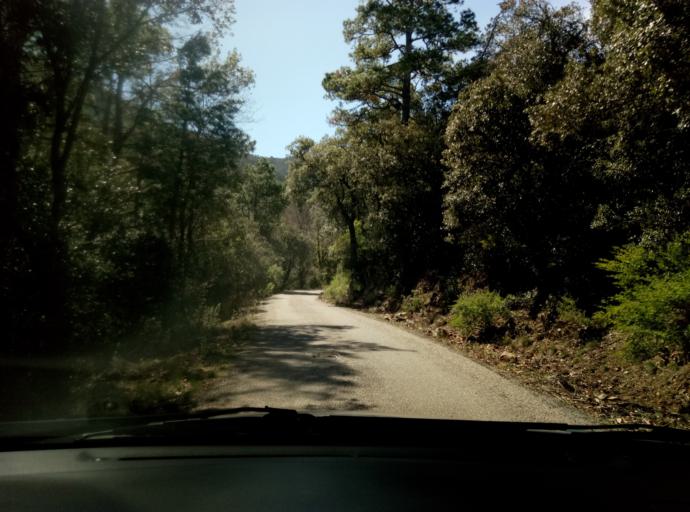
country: ES
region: Catalonia
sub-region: Provincia de Tarragona
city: Capafonts
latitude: 41.3443
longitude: 1.0584
